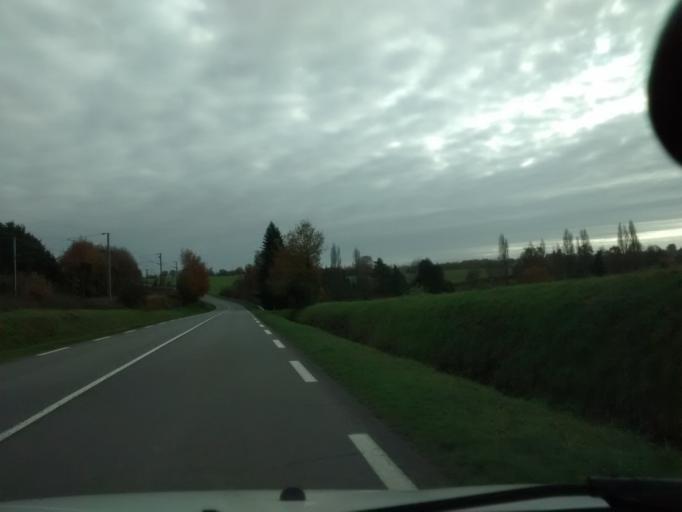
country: FR
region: Brittany
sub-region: Departement d'Ille-et-Vilaine
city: Erbree
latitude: 48.1143
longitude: -1.1354
